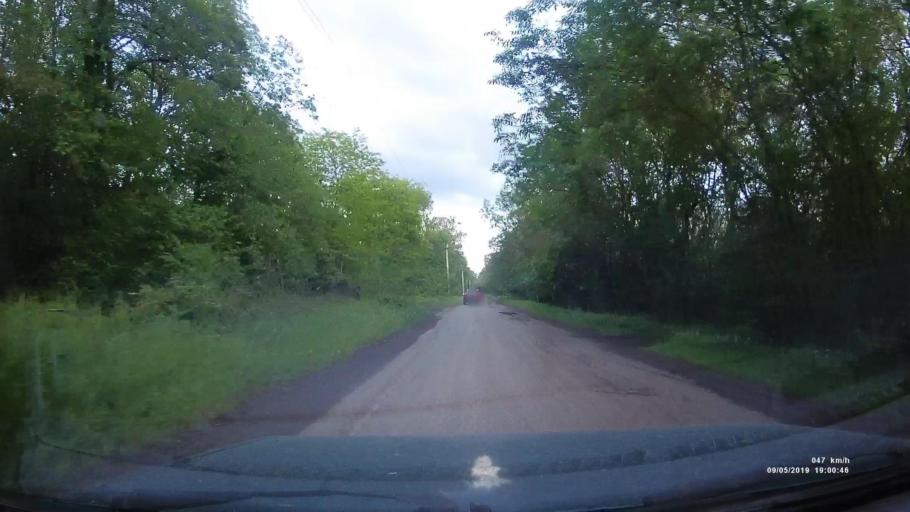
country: RU
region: Krasnodarskiy
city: Kanelovskaya
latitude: 46.7506
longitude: 39.1388
